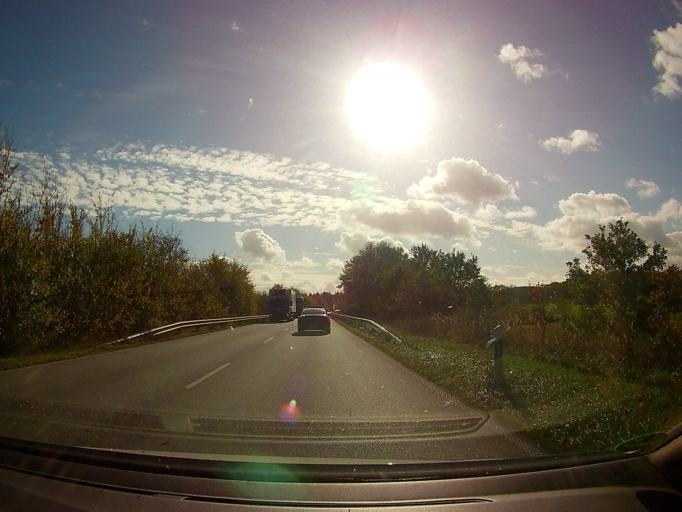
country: DE
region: Schleswig-Holstein
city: Todendorf
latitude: 53.6833
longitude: 10.3800
